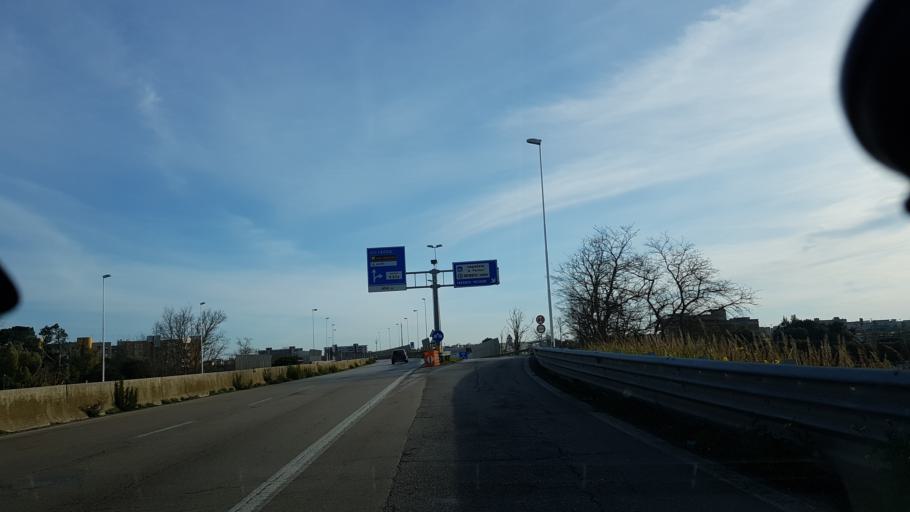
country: IT
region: Apulia
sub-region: Provincia di Brindisi
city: Brindisi
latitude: 40.6293
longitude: 17.9183
